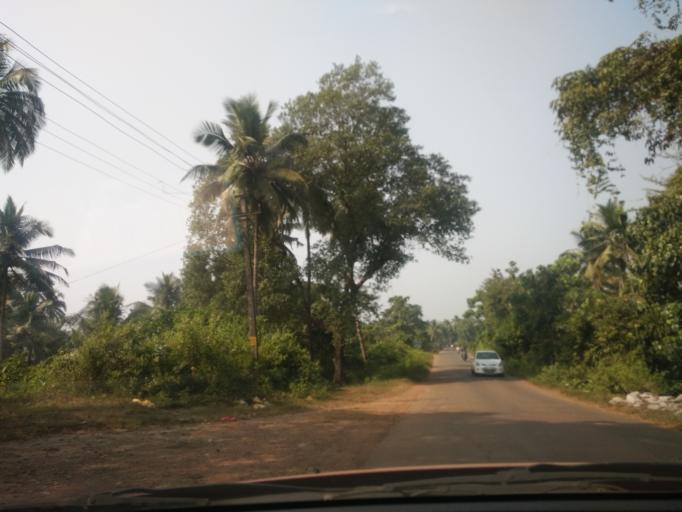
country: IN
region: Goa
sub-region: North Goa
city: Valpoy
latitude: 15.5035
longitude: 74.1386
